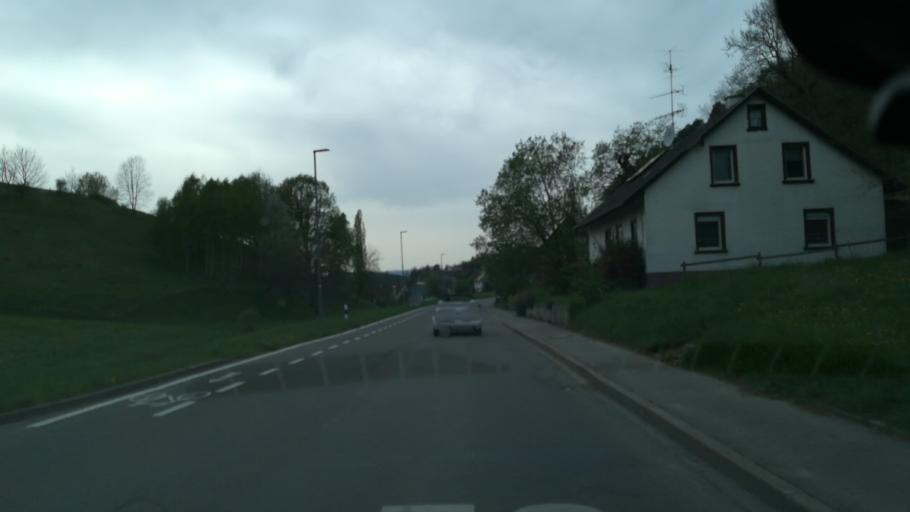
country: DE
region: Baden-Wuerttemberg
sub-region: Freiburg Region
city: Radolfzell am Bodensee
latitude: 47.7738
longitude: 9.0041
